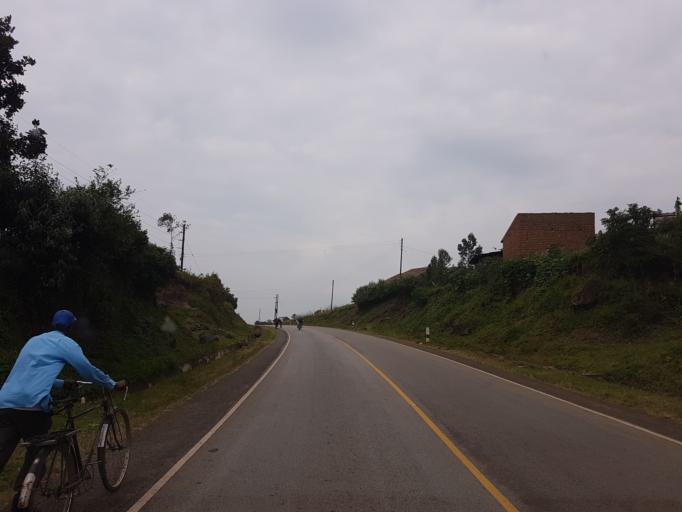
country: UG
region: Western Region
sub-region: Kisoro District
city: Kisoro
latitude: -1.2993
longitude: 29.7215
